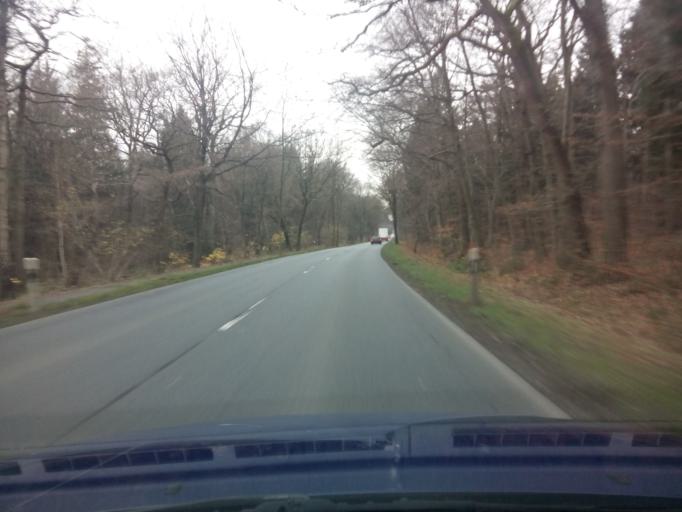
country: DE
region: Lower Saxony
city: Elmlohe
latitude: 53.6182
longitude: 8.7091
